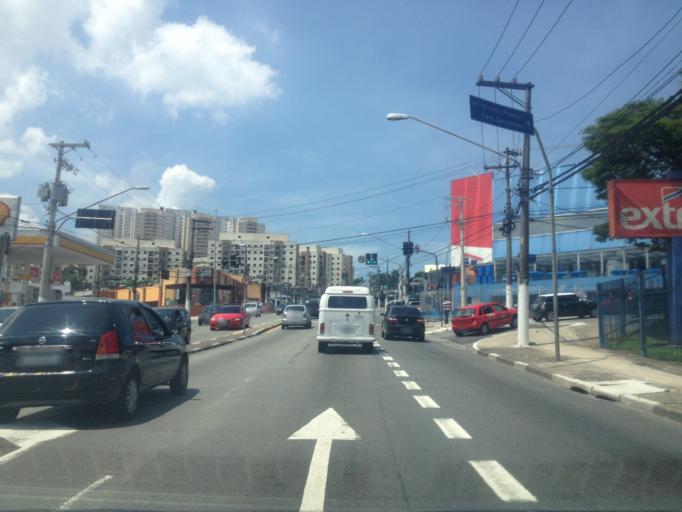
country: BR
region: Sao Paulo
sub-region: Diadema
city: Diadema
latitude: -23.6647
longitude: -46.6784
